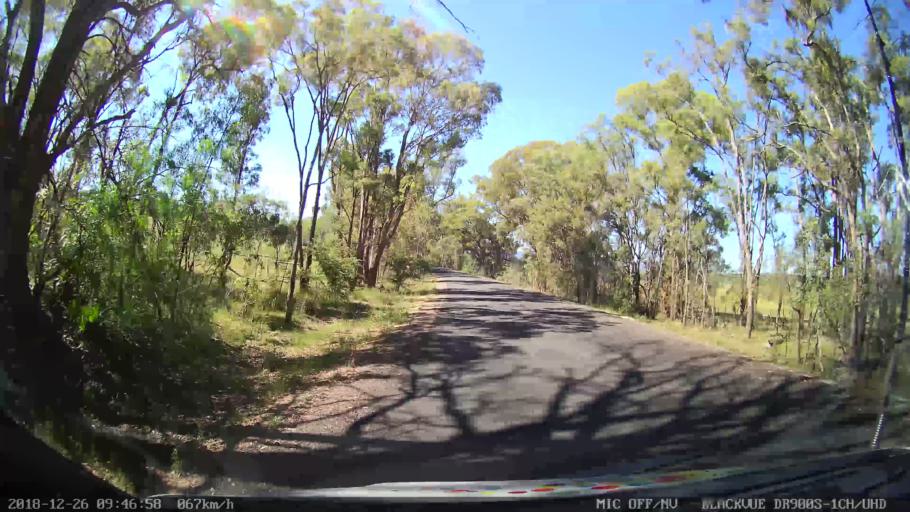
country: AU
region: New South Wales
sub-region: Mid-Western Regional
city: Kandos
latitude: -32.9750
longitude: 150.1043
